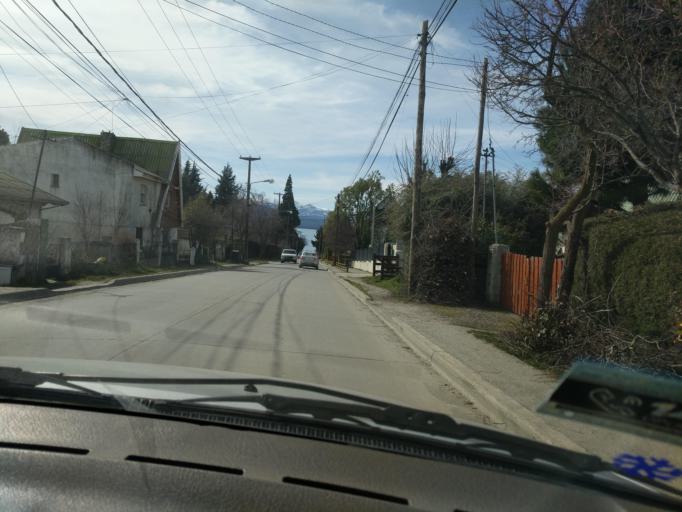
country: AR
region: Rio Negro
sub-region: Departamento de Bariloche
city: San Carlos de Bariloche
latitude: -41.1298
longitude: -71.3560
